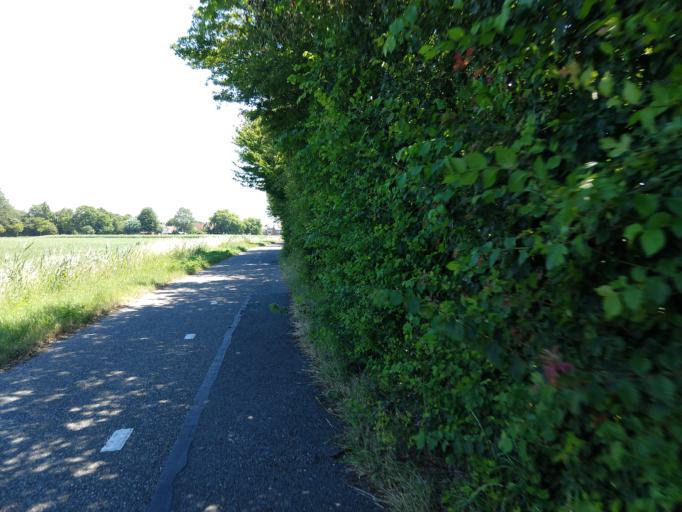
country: NL
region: Zeeland
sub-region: Gemeente Veere
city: Veere
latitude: 51.5429
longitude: 3.6543
